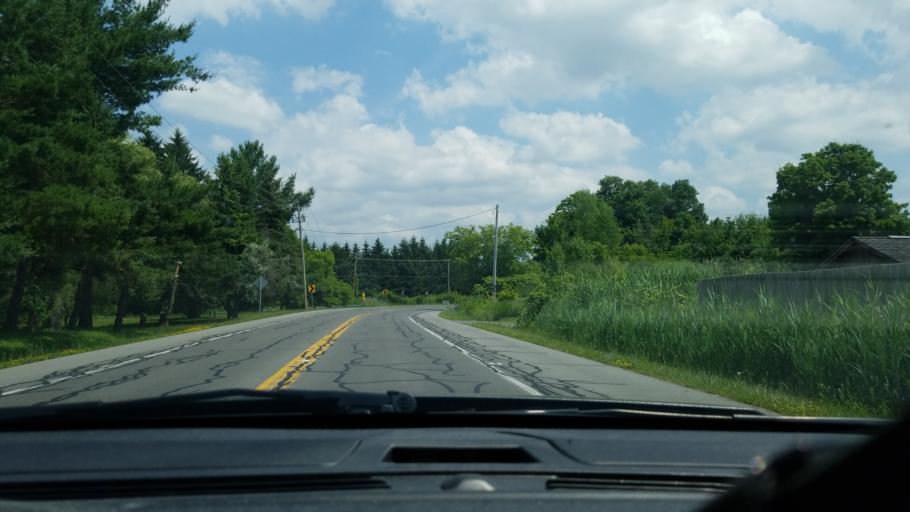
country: US
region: New York
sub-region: Onondaga County
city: North Syracuse
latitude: 43.1492
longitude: -76.1763
